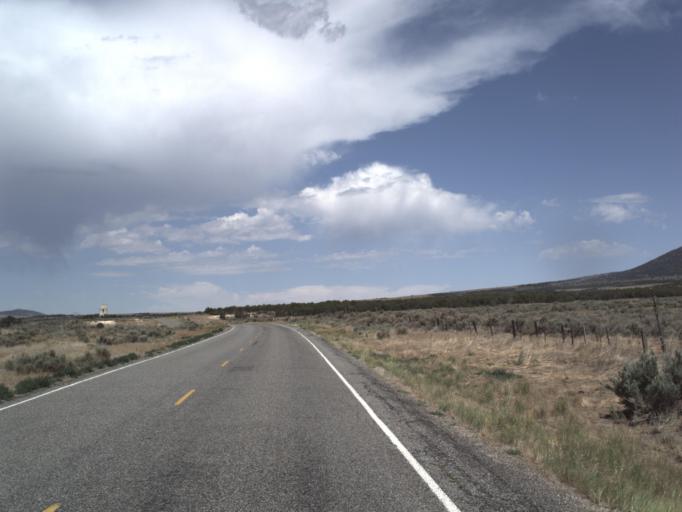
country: US
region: Utah
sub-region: Utah County
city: Genola
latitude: 39.9369
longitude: -112.1791
